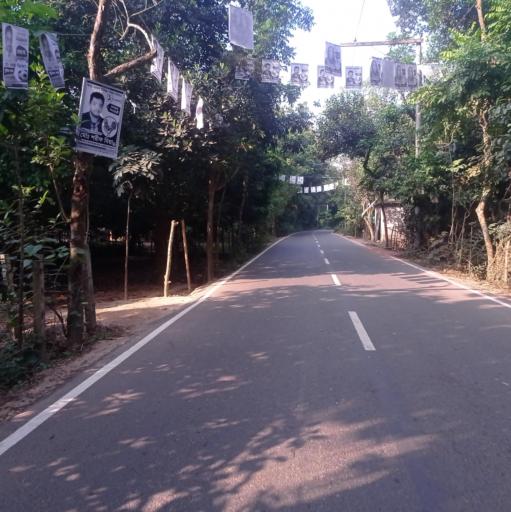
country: BD
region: Dhaka
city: Bhairab Bazar
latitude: 24.0525
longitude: 90.8349
